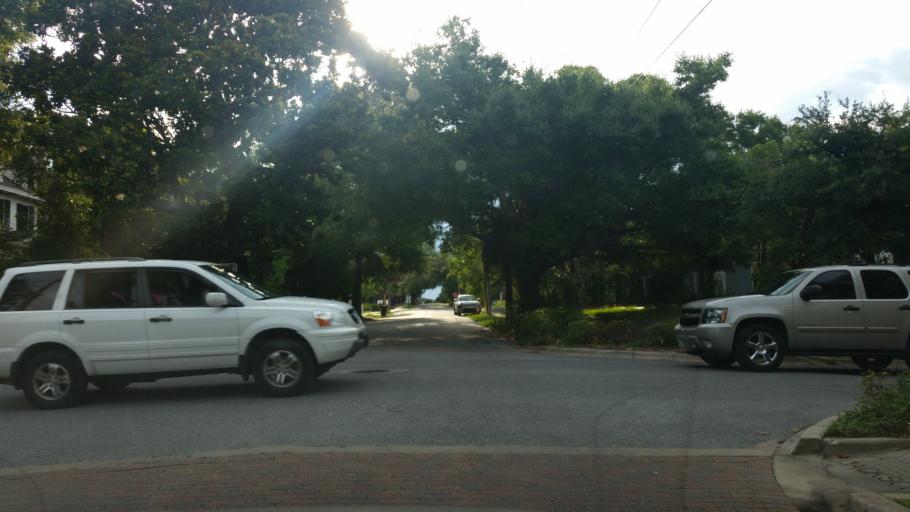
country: US
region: Florida
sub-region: Escambia County
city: Pensacola
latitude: 30.4189
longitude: -87.2198
